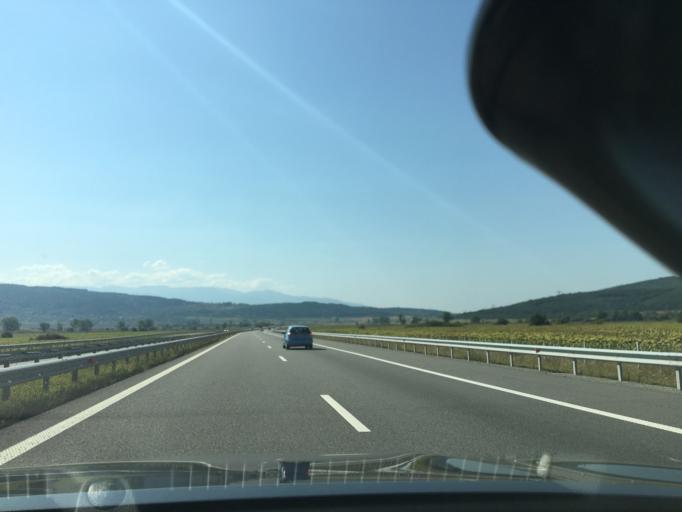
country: BG
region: Kyustendil
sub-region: Obshtina Bobovdol
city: Bobovdol
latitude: 42.4217
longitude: 23.1180
